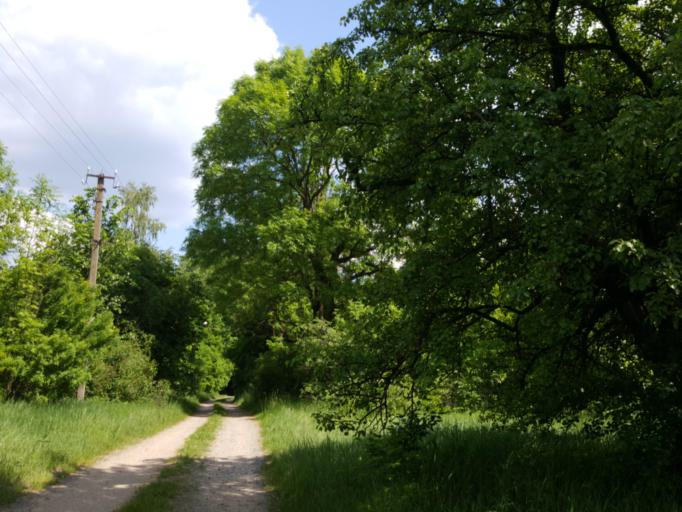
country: PL
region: Podlasie
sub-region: Powiat hajnowski
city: Hajnowka
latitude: 52.5662
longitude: 23.6093
